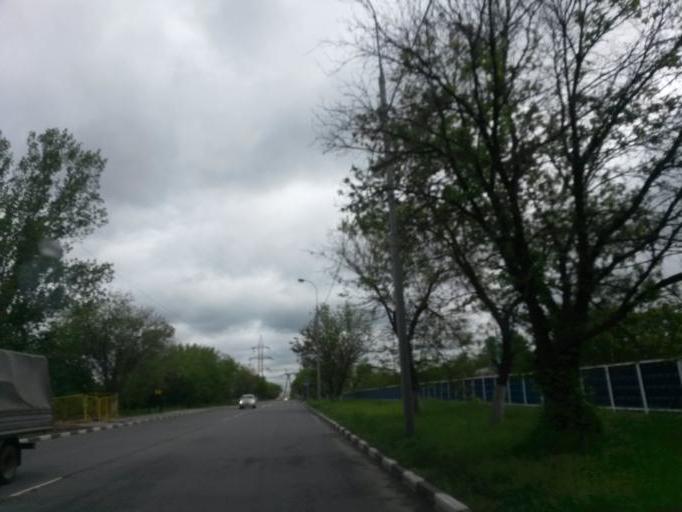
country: RU
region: Moscow
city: Kapotnya
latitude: 55.6479
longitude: 37.7891
